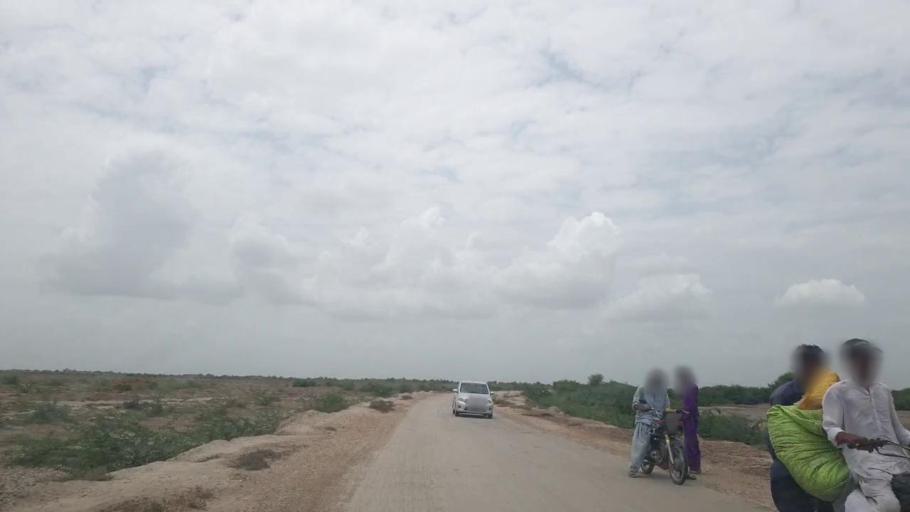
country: PK
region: Sindh
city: Naukot
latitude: 24.9510
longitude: 69.2823
